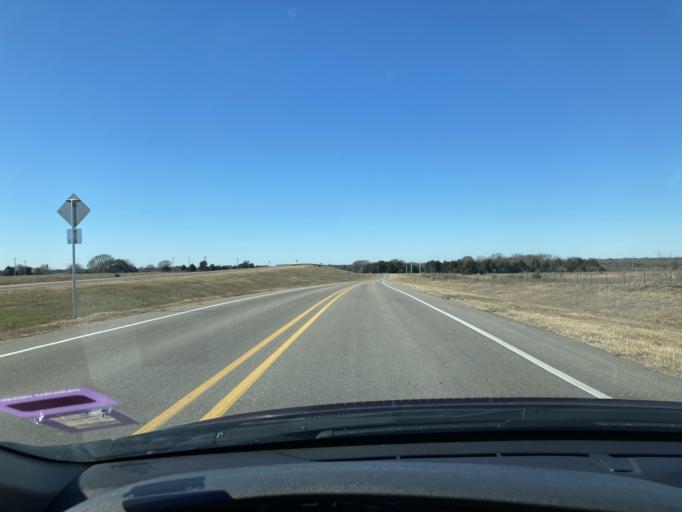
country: US
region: Texas
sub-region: Navarro County
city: Corsicana
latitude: 32.0483
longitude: -96.4921
